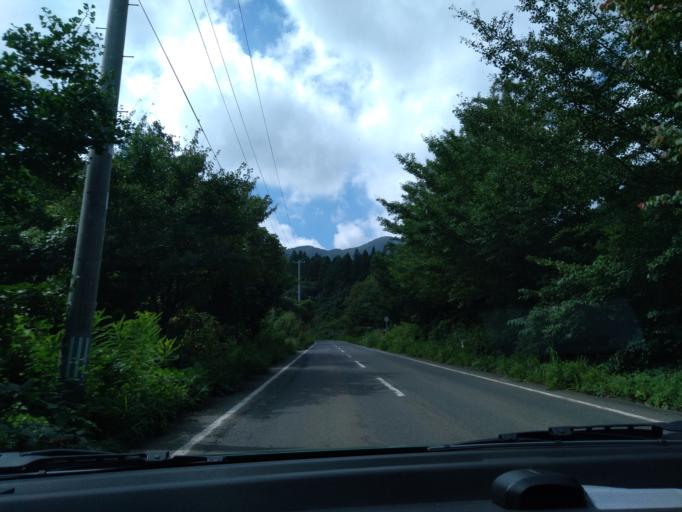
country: JP
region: Iwate
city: Morioka-shi
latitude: 39.6346
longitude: 141.0892
